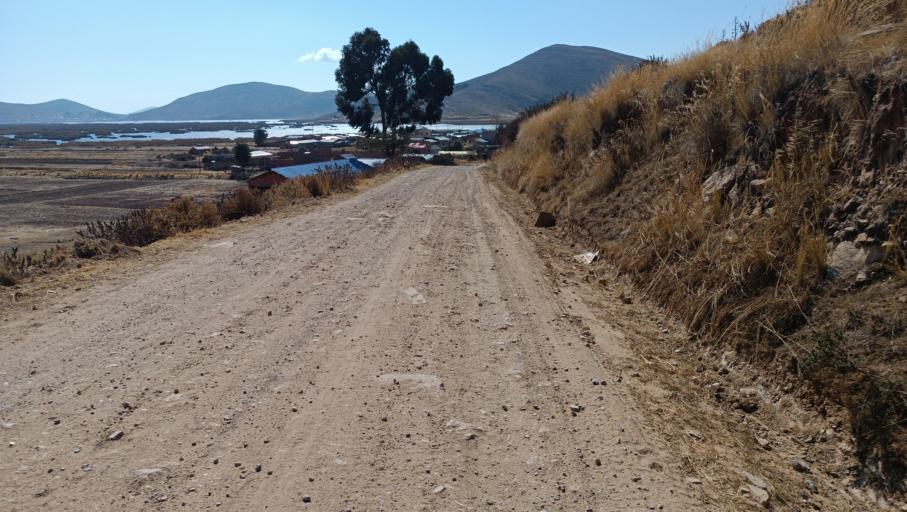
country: BO
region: La Paz
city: Huatajata
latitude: -16.3468
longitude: -68.6744
